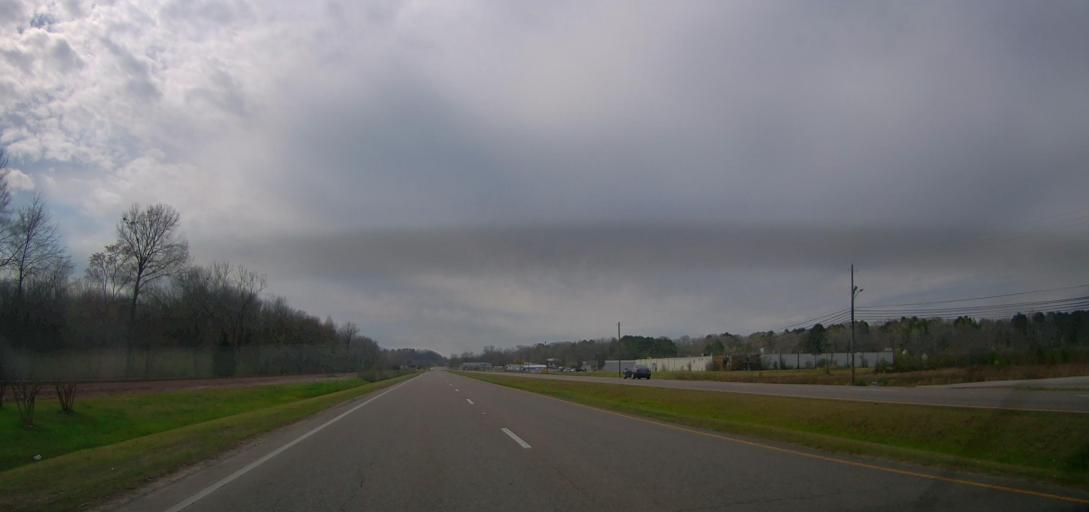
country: US
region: Alabama
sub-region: Walker County
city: Carbon Hill
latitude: 33.8842
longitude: -87.5168
